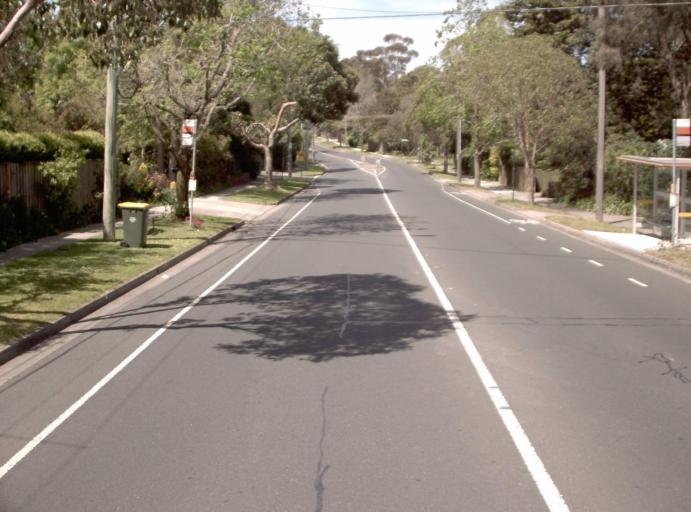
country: AU
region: Victoria
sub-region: Whitehorse
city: Blackburn
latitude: -37.8265
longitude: 145.1526
